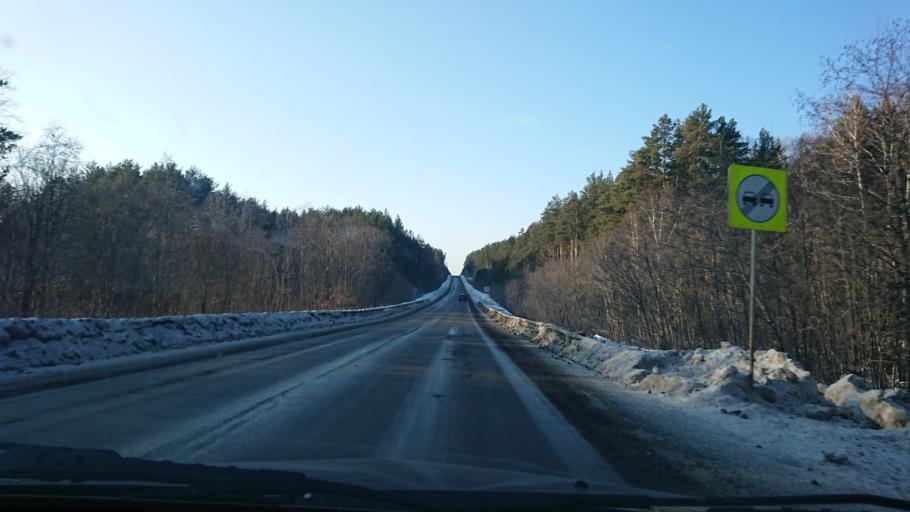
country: RU
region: Sverdlovsk
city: Gornyy Shchit
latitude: 56.6327
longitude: 60.3249
